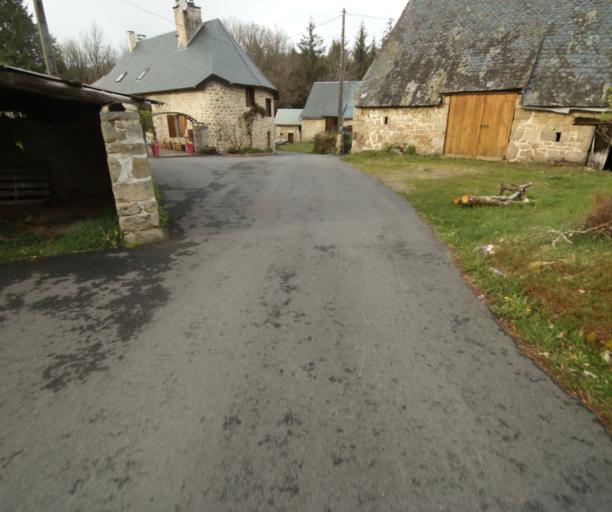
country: FR
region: Limousin
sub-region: Departement de la Correze
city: Argentat
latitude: 45.2005
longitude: 1.9810
